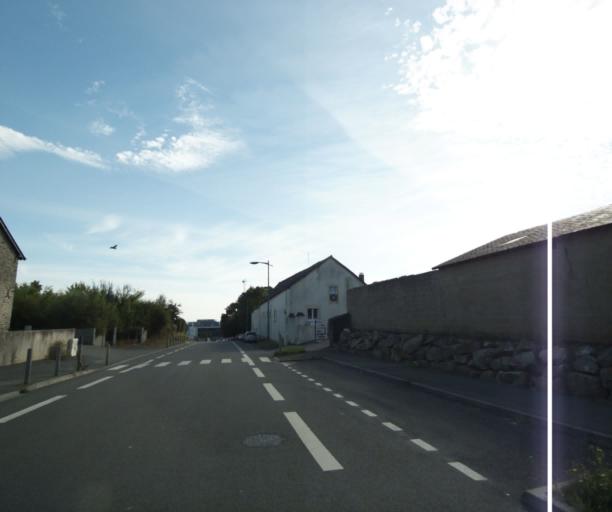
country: FR
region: Pays de la Loire
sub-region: Departement de la Mayenne
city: Laval
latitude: 48.0562
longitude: -0.7882
